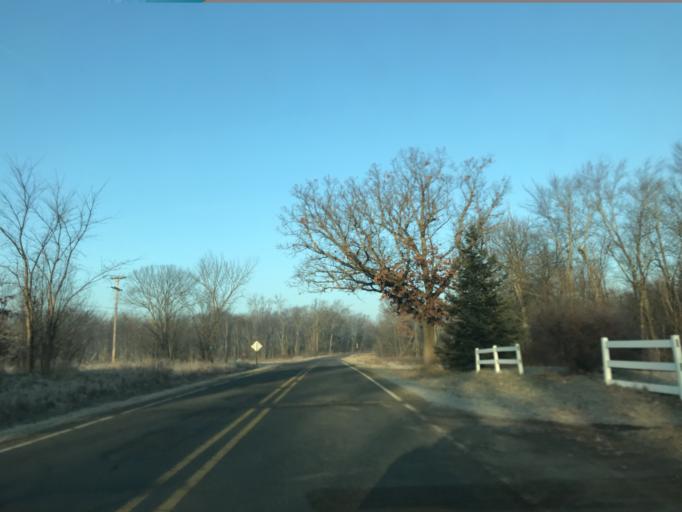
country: US
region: Michigan
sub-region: Ingham County
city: Leslie
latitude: 42.4023
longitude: -84.4828
